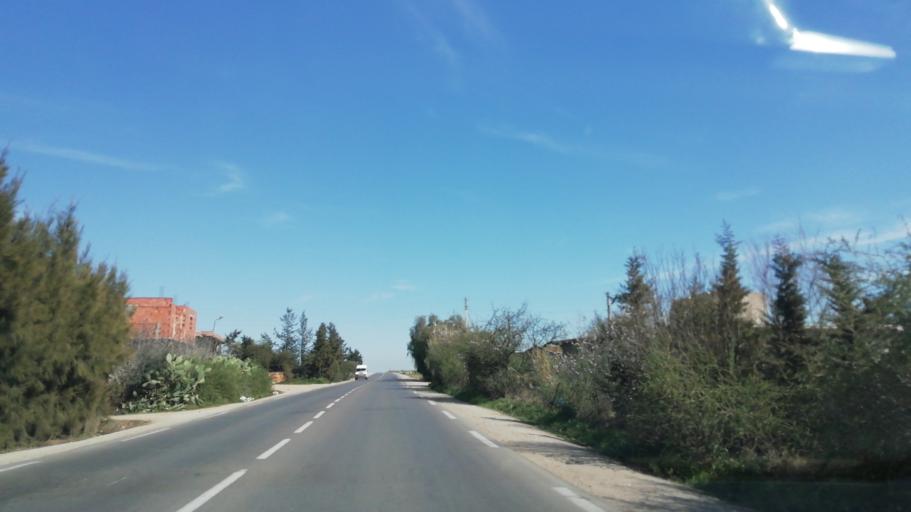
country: DZ
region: Mascara
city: Mascara
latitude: 35.4149
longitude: 0.3919
